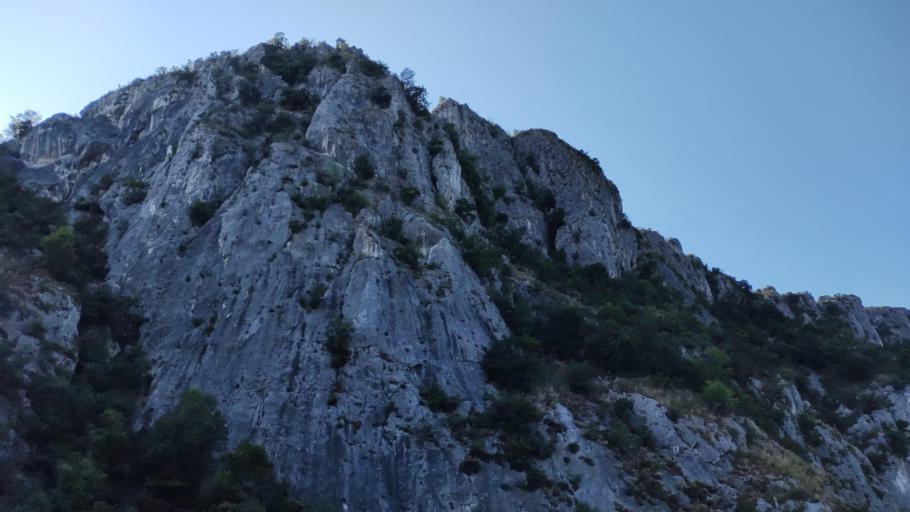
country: RO
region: Mehedinti
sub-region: Comuna Dubova
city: Dubova
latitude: 44.5892
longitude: 22.2577
